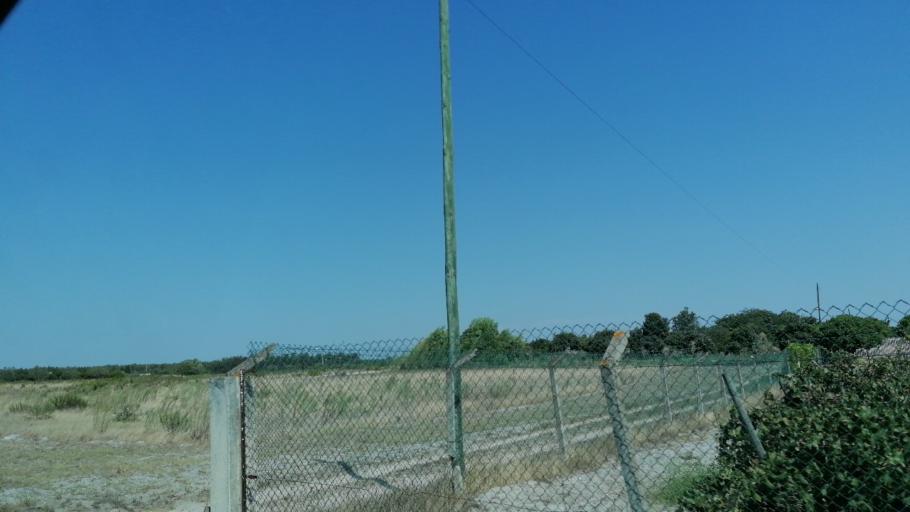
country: PT
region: Santarem
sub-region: Benavente
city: Poceirao
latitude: 38.7062
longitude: -8.7197
